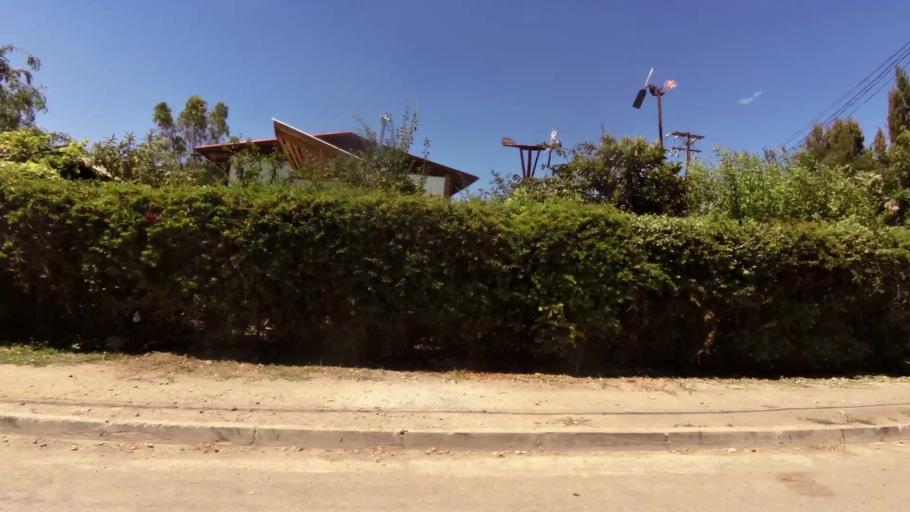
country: CL
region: O'Higgins
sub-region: Provincia de Cachapoal
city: Rancagua
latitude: -34.2253
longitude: -70.7873
